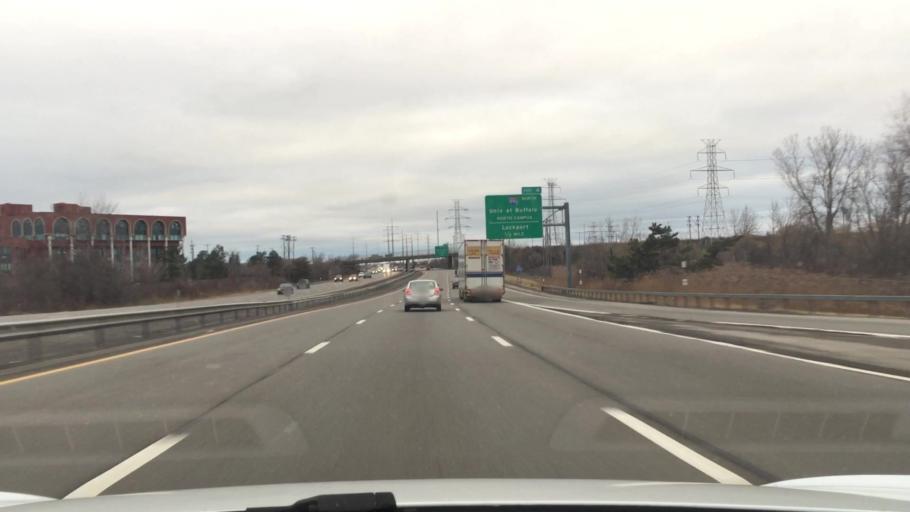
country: US
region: New York
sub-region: Erie County
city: Amherst
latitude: 42.9876
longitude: -78.7969
